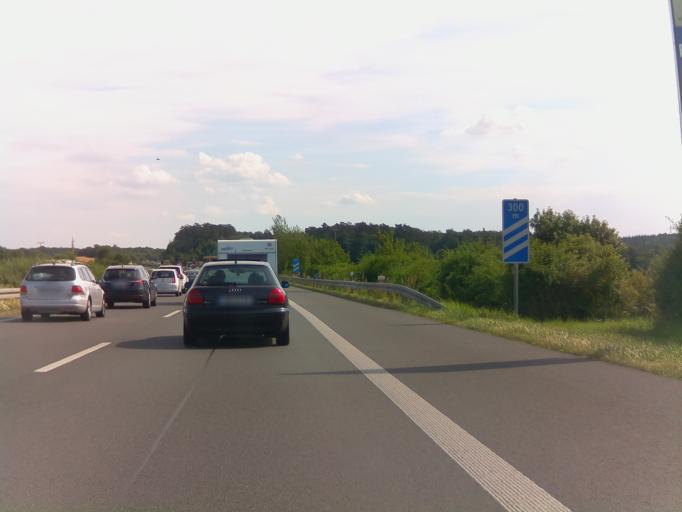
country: DE
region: Baden-Wuerttemberg
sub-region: Regierungsbezirk Stuttgart
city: Grossrinderfeld
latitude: 49.6349
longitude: 9.7300
